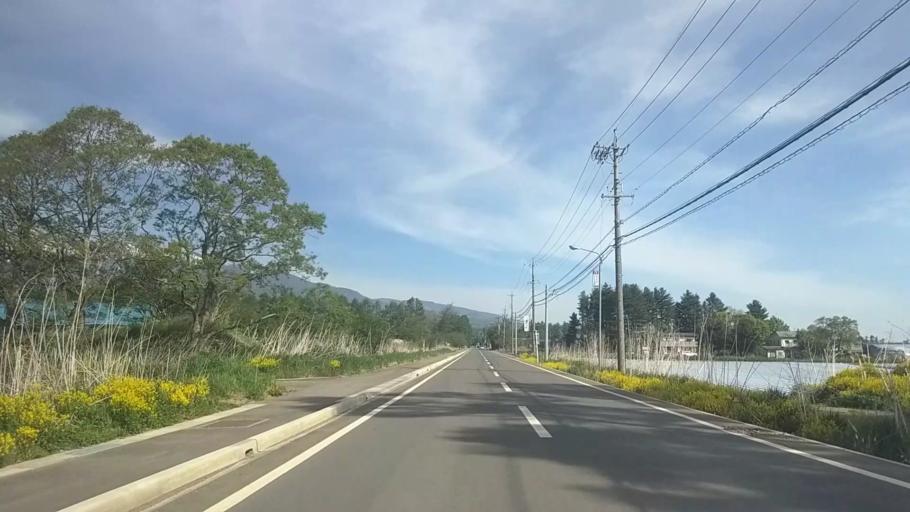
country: JP
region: Yamanashi
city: Nirasaki
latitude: 35.9473
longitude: 138.4773
